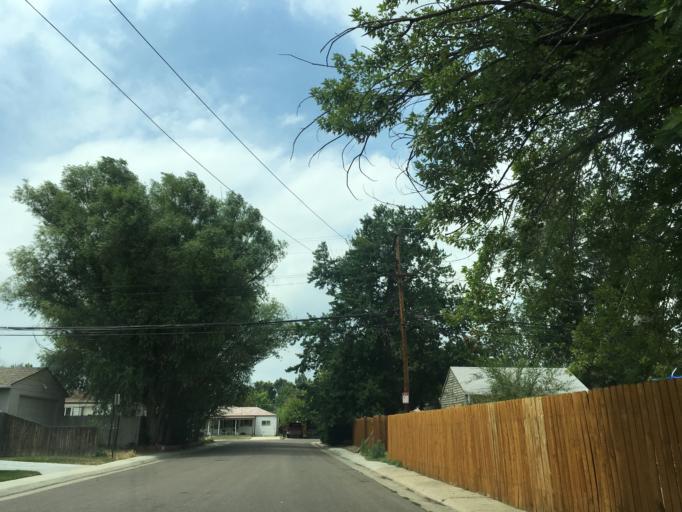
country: US
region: Colorado
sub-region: Arapahoe County
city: Sheridan
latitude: 39.6803
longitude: -105.0277
